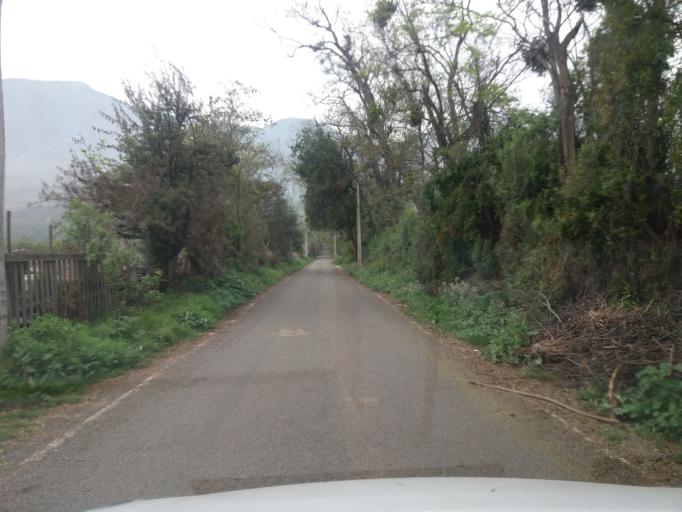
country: CL
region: Valparaiso
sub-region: Provincia de San Felipe
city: Llaillay
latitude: -32.8466
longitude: -71.0629
